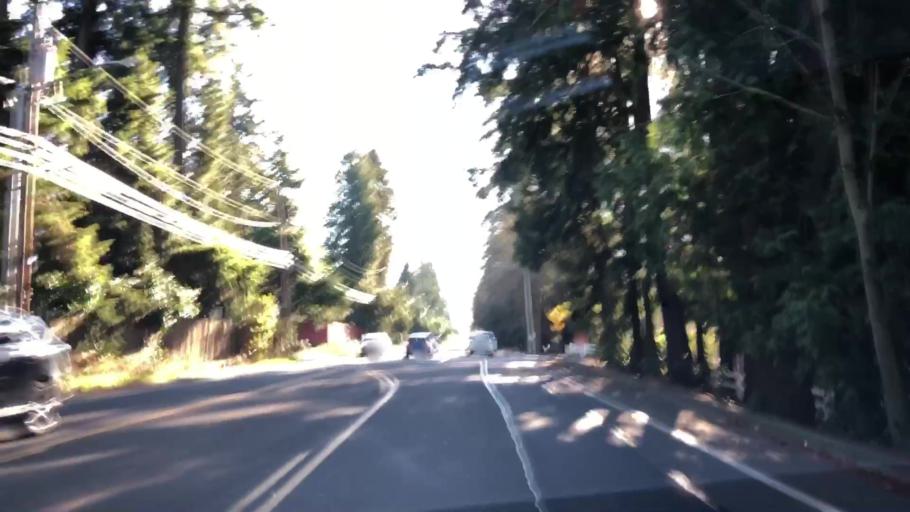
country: US
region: Washington
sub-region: King County
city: Kingsgate
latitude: 47.7017
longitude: -122.1758
